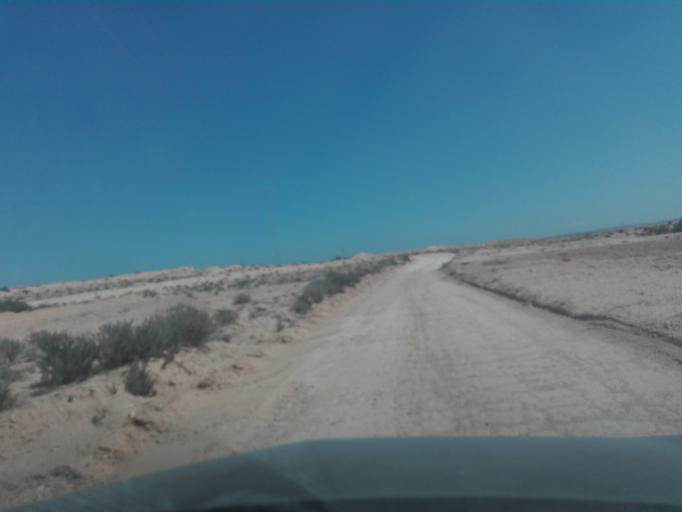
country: TN
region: Qabis
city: Gabes
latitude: 33.8447
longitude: 9.9877
